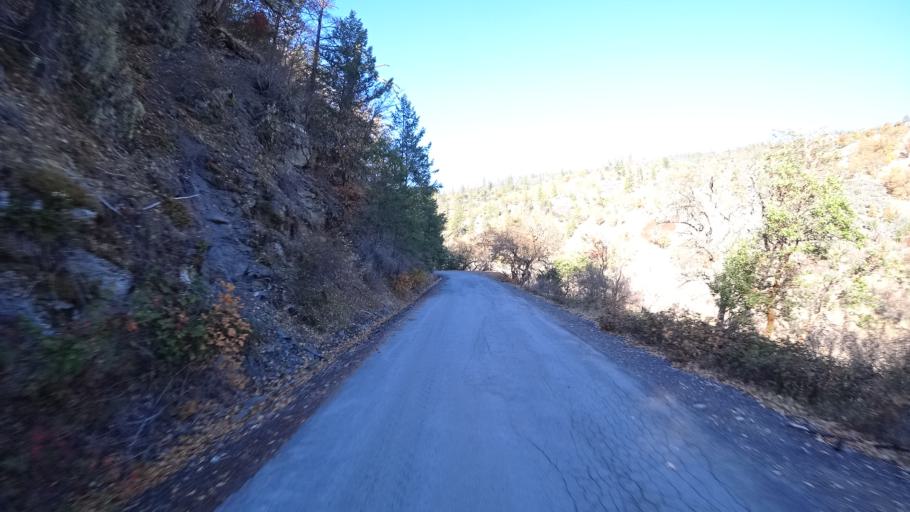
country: US
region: California
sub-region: Siskiyou County
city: Yreka
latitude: 41.8460
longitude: -122.9034
